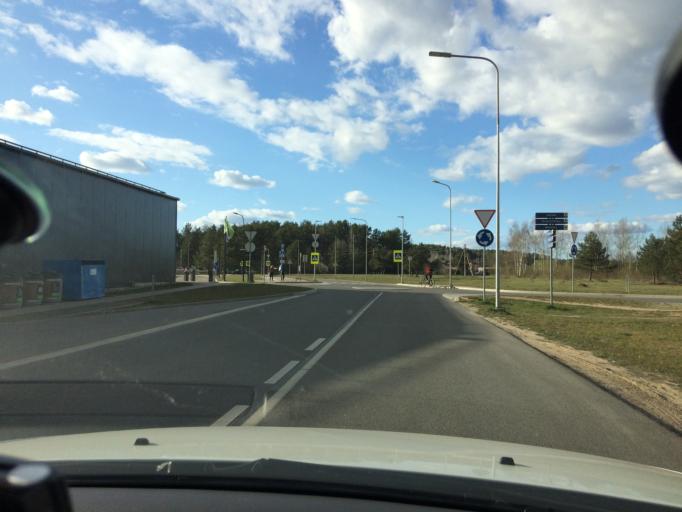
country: LT
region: Vilnius County
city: Rasos
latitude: 54.7779
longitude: 25.3430
